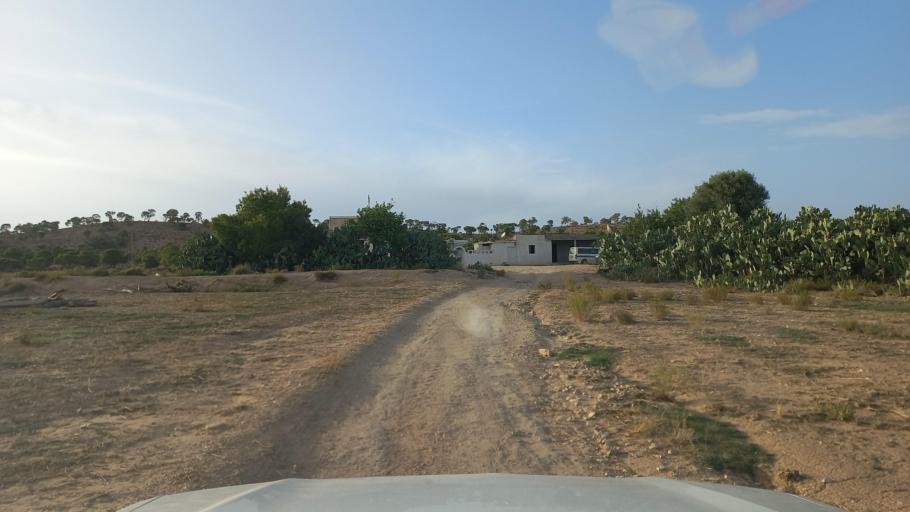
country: TN
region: Al Qasrayn
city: Sbiba
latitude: 35.4042
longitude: 8.8959
